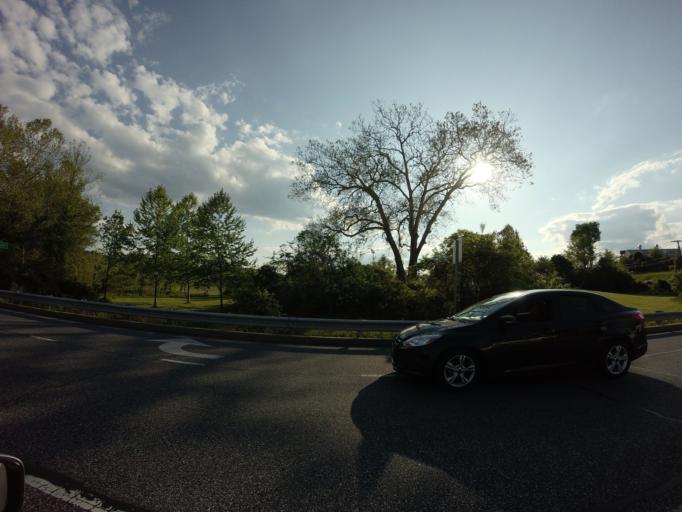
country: US
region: Maryland
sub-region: Baltimore County
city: Mays Chapel
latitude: 39.4201
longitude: -76.6701
